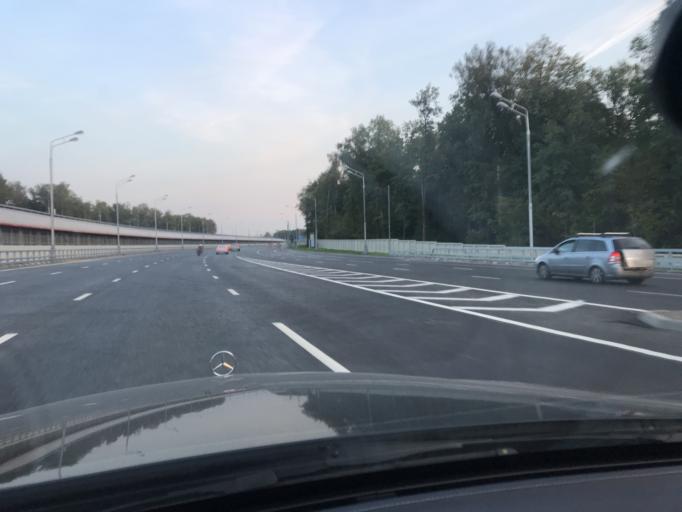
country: RU
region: Moskovskaya
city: Mosrentgen
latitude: 55.5820
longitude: 37.4441
